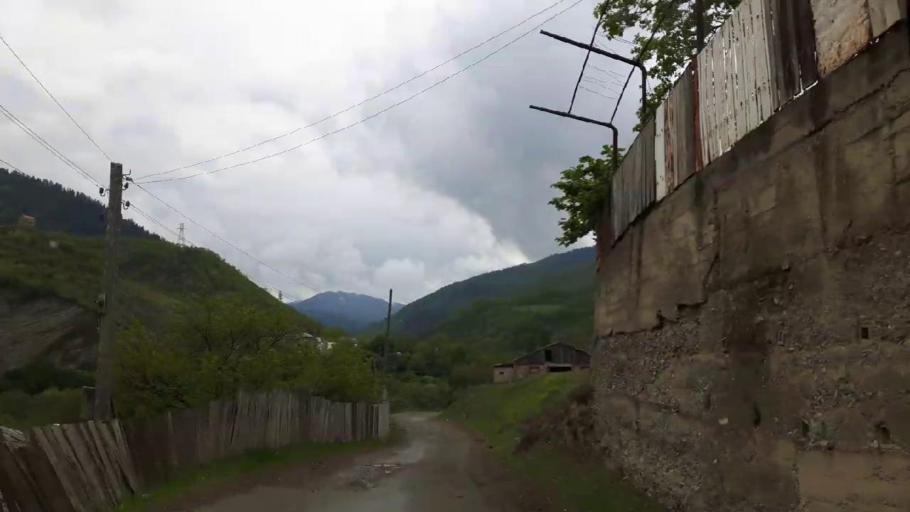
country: GE
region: Shida Kartli
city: Gori
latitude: 41.8893
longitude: 44.0046
